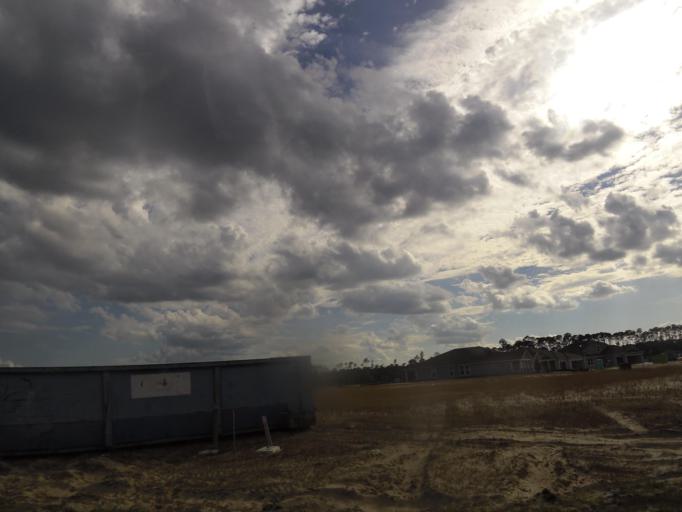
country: US
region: Florida
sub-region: Saint Johns County
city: Palm Valley
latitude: 30.1776
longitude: -81.5090
